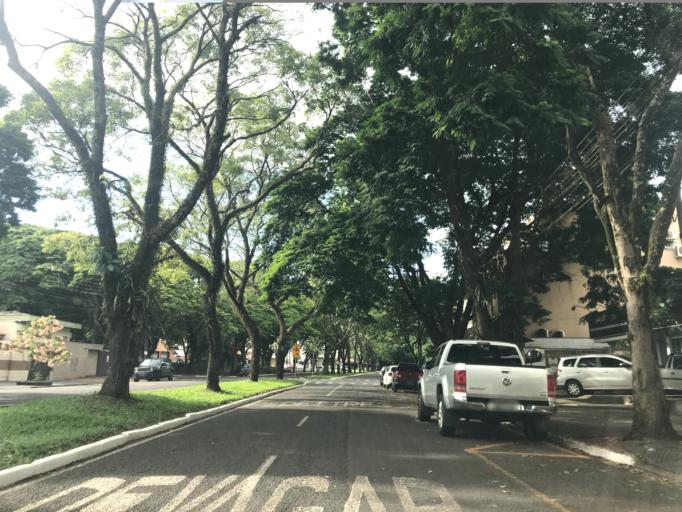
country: BR
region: Parana
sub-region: Maringa
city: Maringa
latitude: -23.4302
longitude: -51.9512
